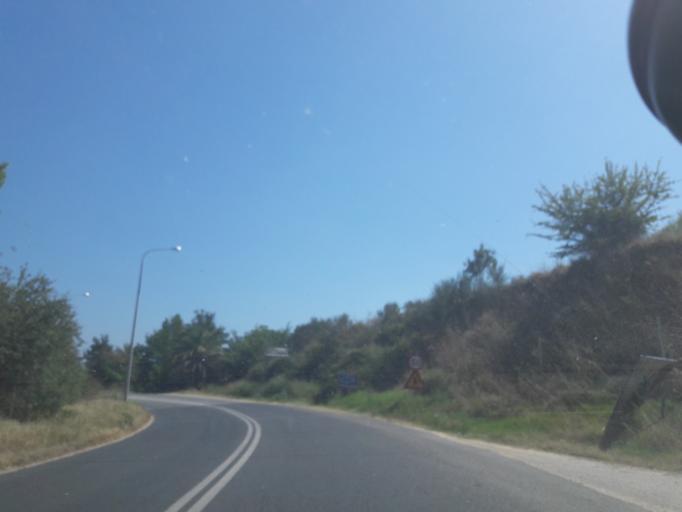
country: GR
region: Central Macedonia
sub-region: Nomos Chalkidikis
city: Nea Roda
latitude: 40.3660
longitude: 23.9177
